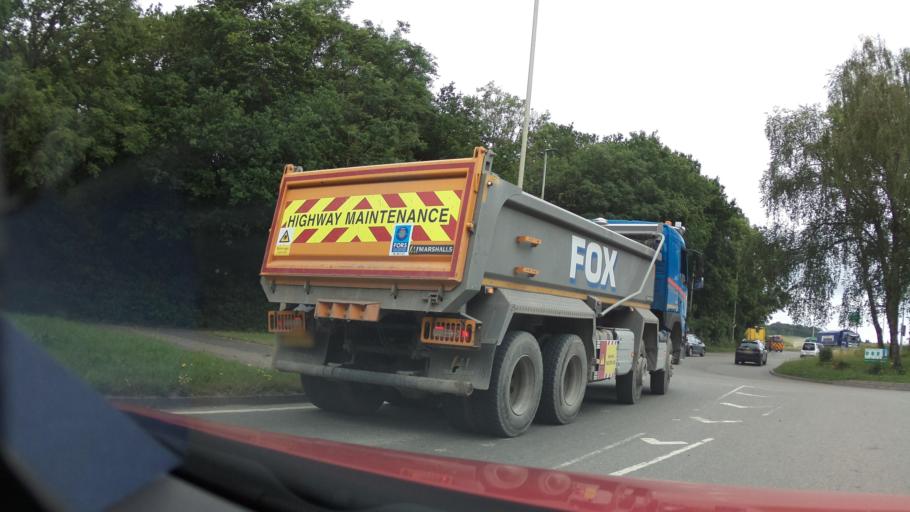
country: GB
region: England
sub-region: Leicestershire
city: Coalville
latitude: 52.7031
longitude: -1.3243
